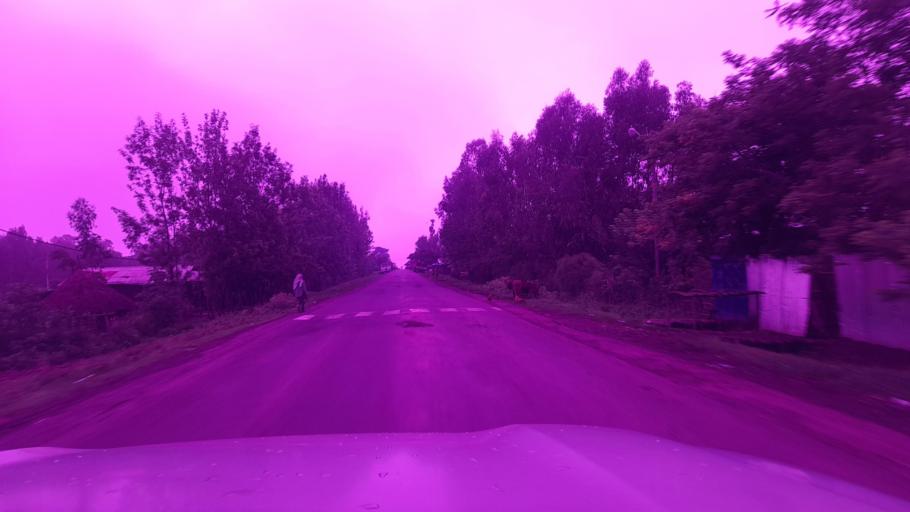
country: ET
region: Oromiya
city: Waliso
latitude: 8.1744
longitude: 37.5691
